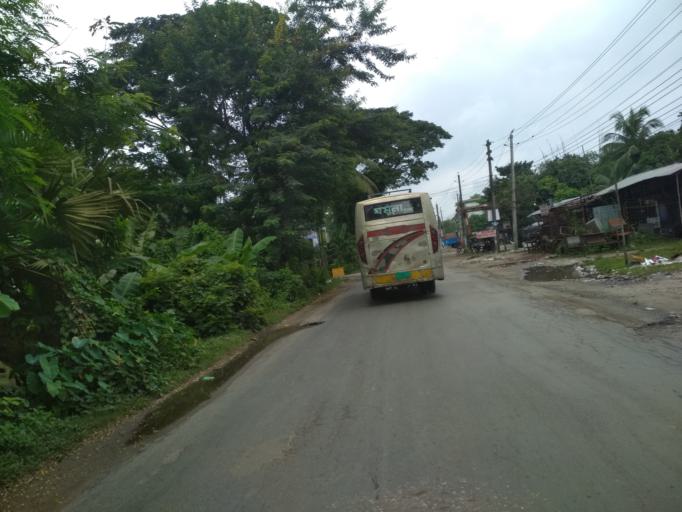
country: BD
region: Chittagong
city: Lakshmipur
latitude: 22.9457
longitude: 90.8189
